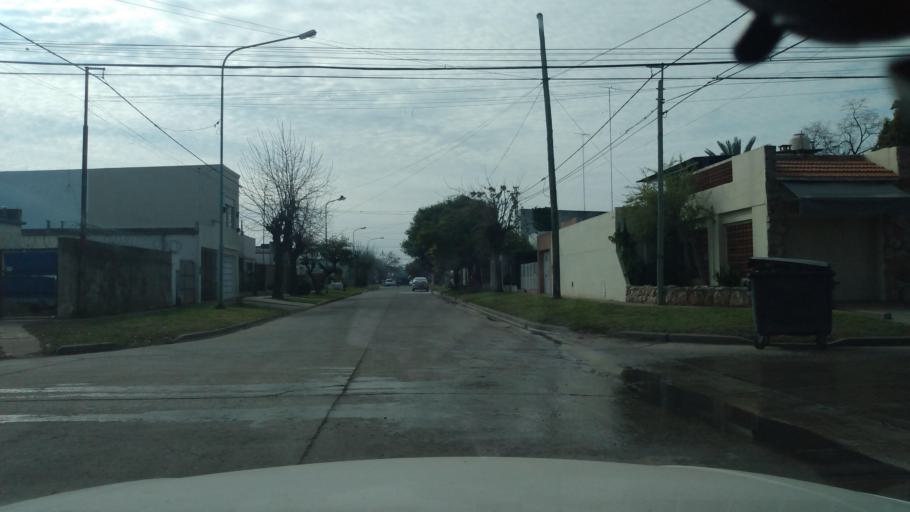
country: AR
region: Buenos Aires
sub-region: Partido de Lujan
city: Lujan
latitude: -34.5774
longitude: -59.1251
